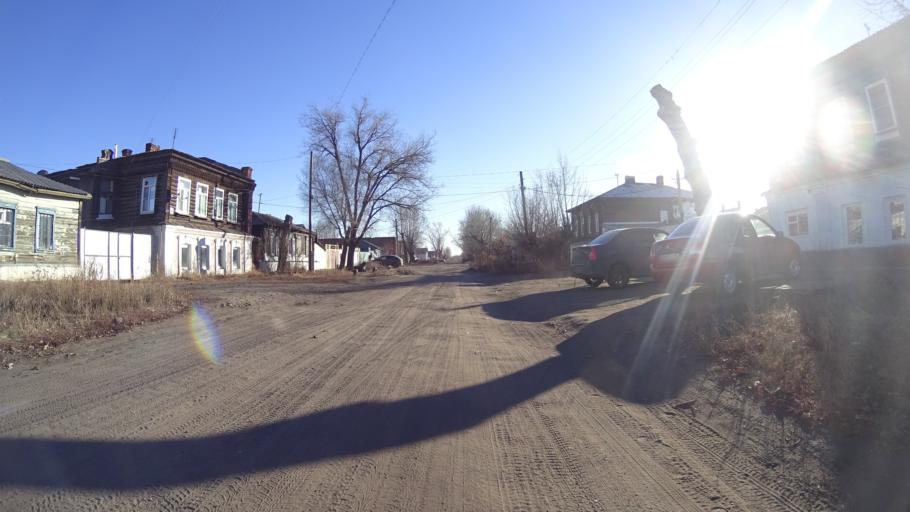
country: RU
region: Chelyabinsk
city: Troitsk
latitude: 54.0871
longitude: 61.5680
